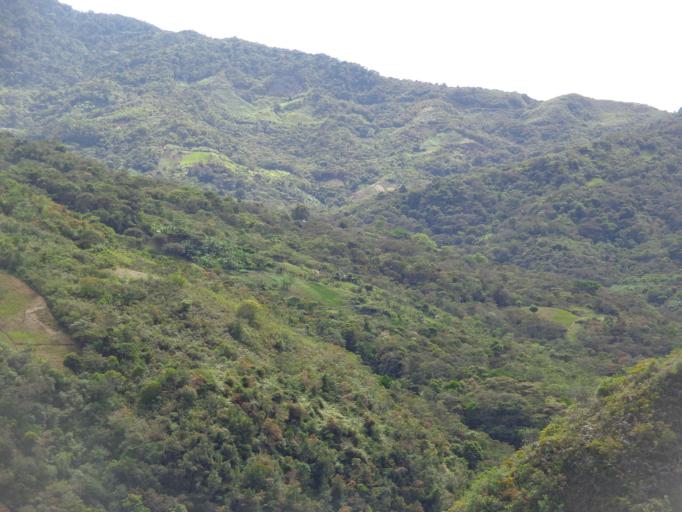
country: BO
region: La Paz
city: Coroico
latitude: -16.2639
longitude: -67.7110
